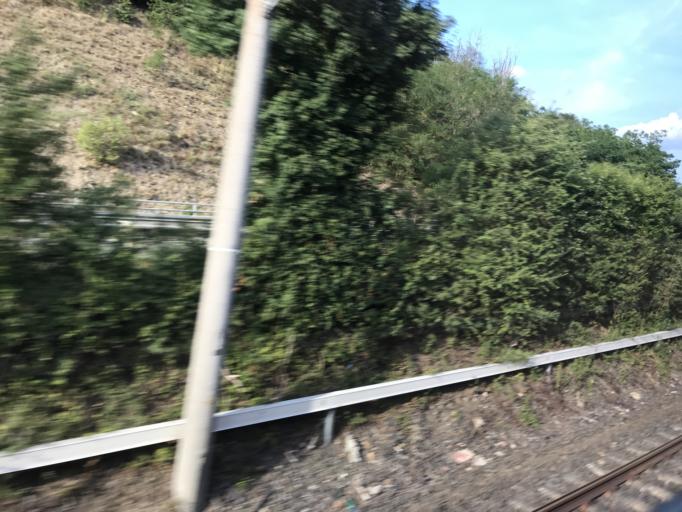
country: DE
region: Hesse
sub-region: Regierungsbezirk Giessen
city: Villmar
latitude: 50.3482
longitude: 8.1990
